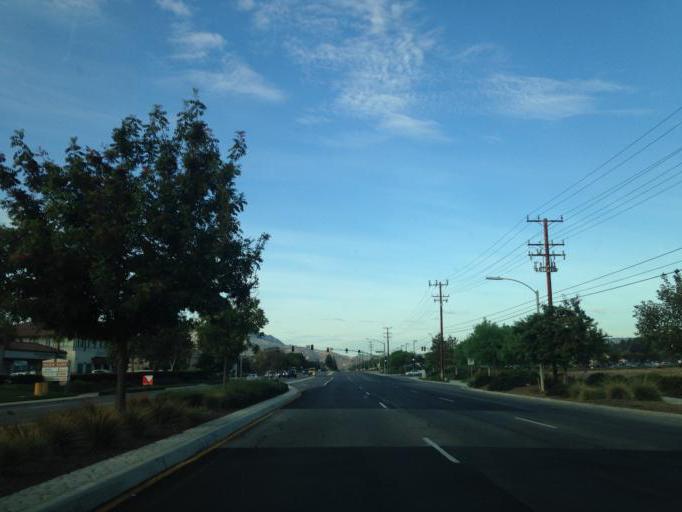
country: US
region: California
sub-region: Riverside County
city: Temecula
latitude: 33.4798
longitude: -117.1038
